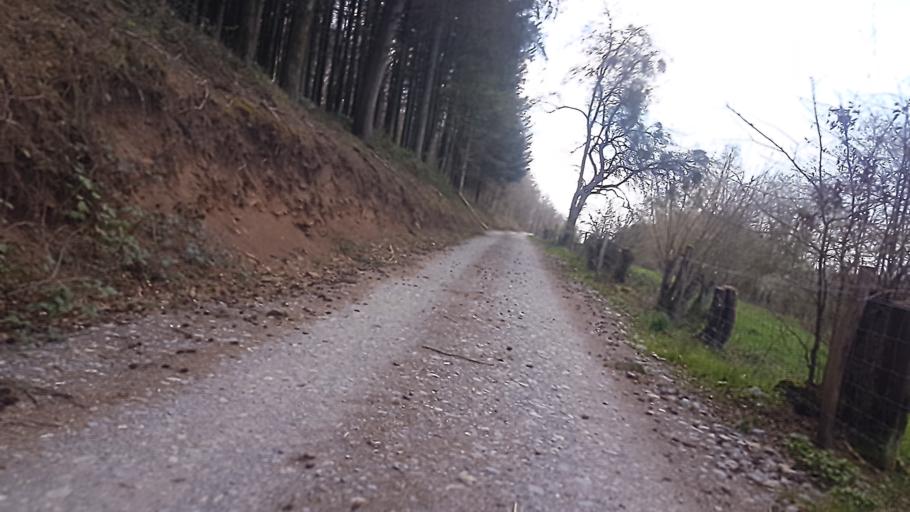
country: BE
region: Wallonia
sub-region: Province de Namur
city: Couvin
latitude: 50.0700
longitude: 4.5949
